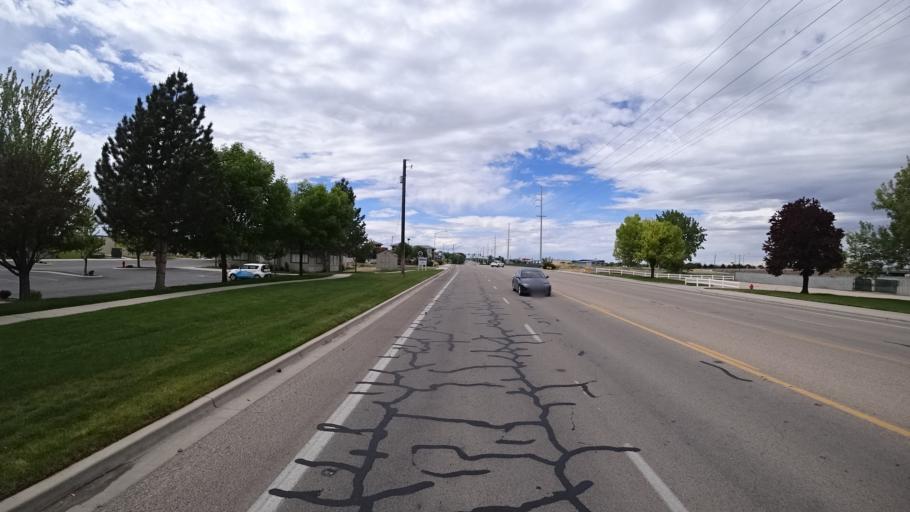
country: US
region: Idaho
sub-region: Ada County
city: Meridian
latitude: 43.5903
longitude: -116.3717
